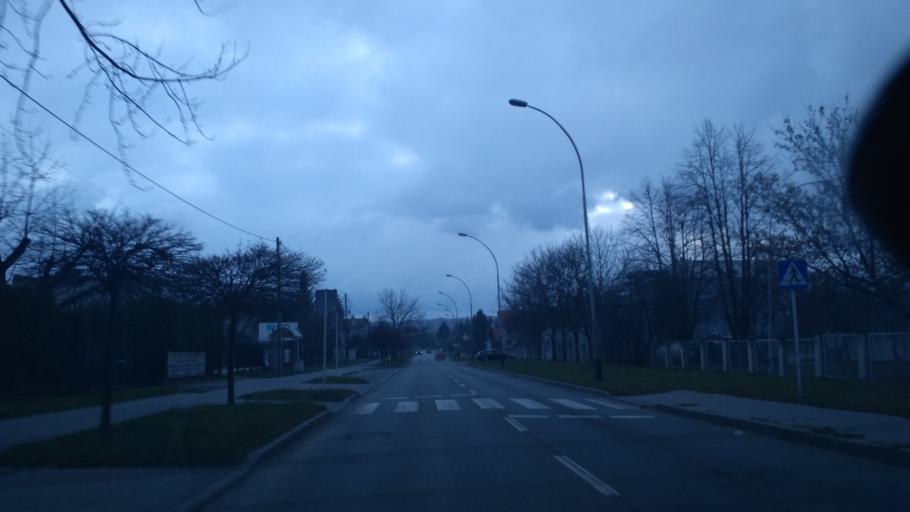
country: PL
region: Subcarpathian Voivodeship
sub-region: Rzeszow
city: Rzeszow
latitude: 50.0346
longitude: 22.0411
